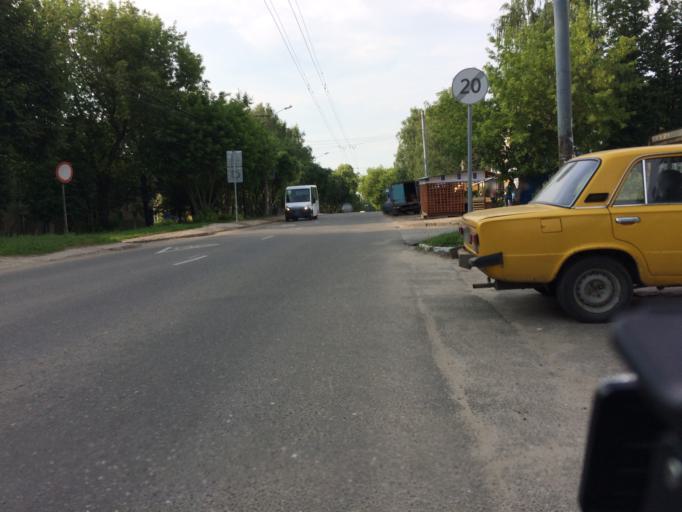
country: RU
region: Mariy-El
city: Yoshkar-Ola
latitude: 56.6250
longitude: 47.9464
